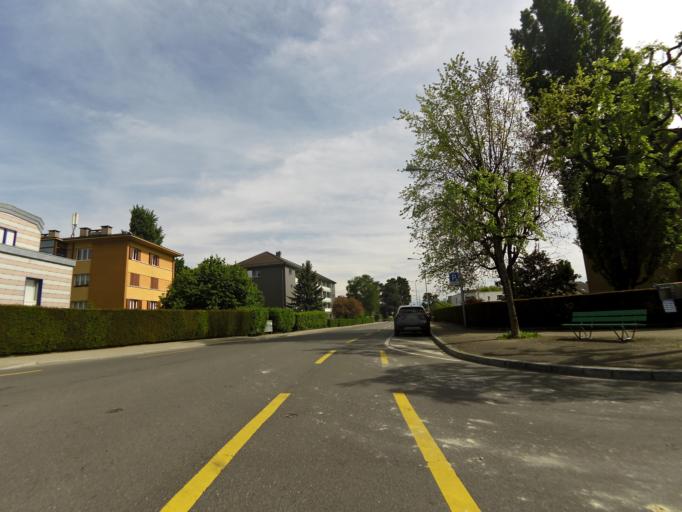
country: CH
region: Vaud
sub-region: Nyon District
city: Nyon
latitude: 46.3933
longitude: 6.2308
